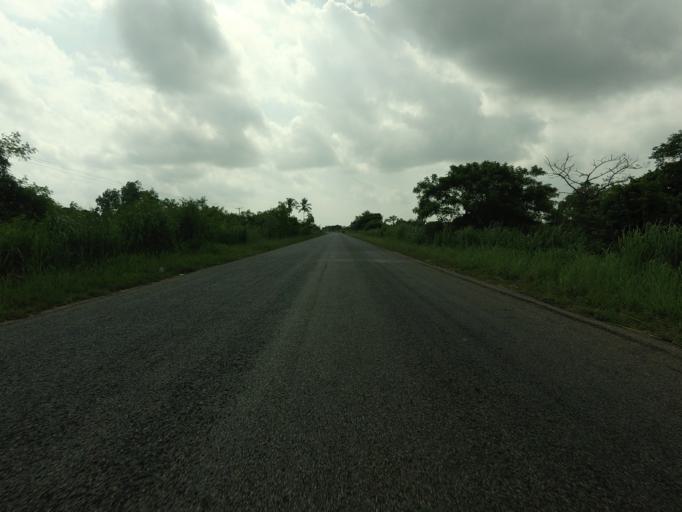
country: GH
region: Volta
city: Ho
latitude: 6.4356
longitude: 0.7304
